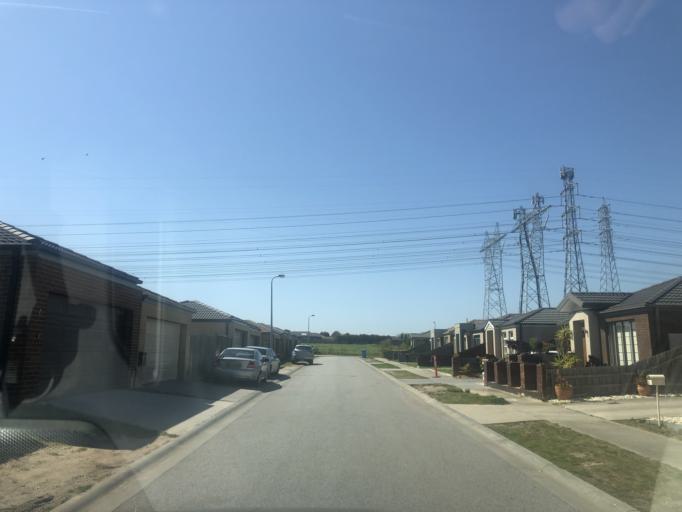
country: AU
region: Victoria
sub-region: Casey
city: Narre Warren South
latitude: -38.0500
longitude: 145.2805
